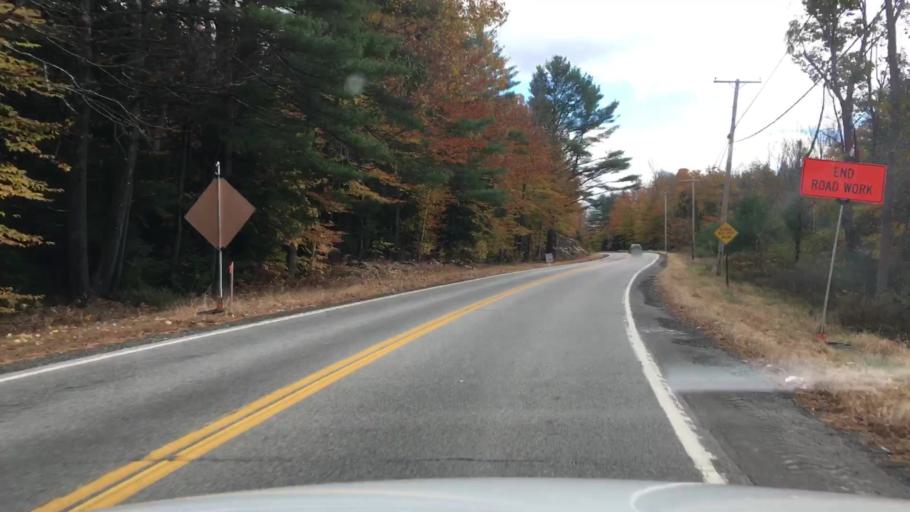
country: US
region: Maine
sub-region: Sagadahoc County
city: Richmond
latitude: 44.0981
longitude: -69.8609
